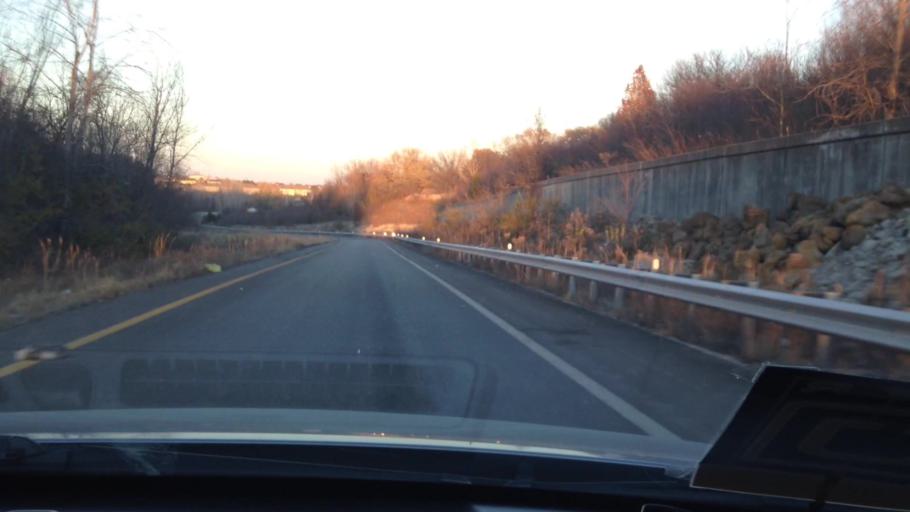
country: US
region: Missouri
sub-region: Clay County
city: Gladstone
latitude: 39.2572
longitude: -94.5871
